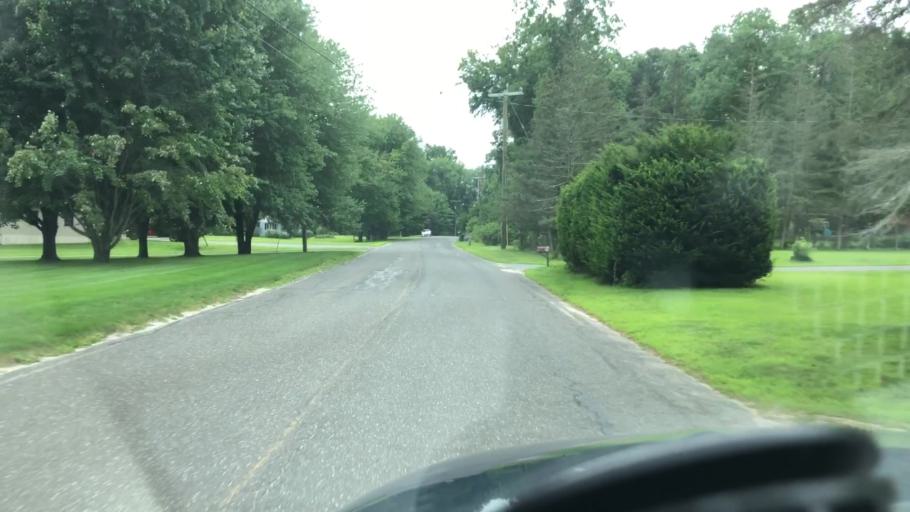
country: US
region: Massachusetts
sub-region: Hampshire County
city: Easthampton
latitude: 42.2430
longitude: -72.6934
